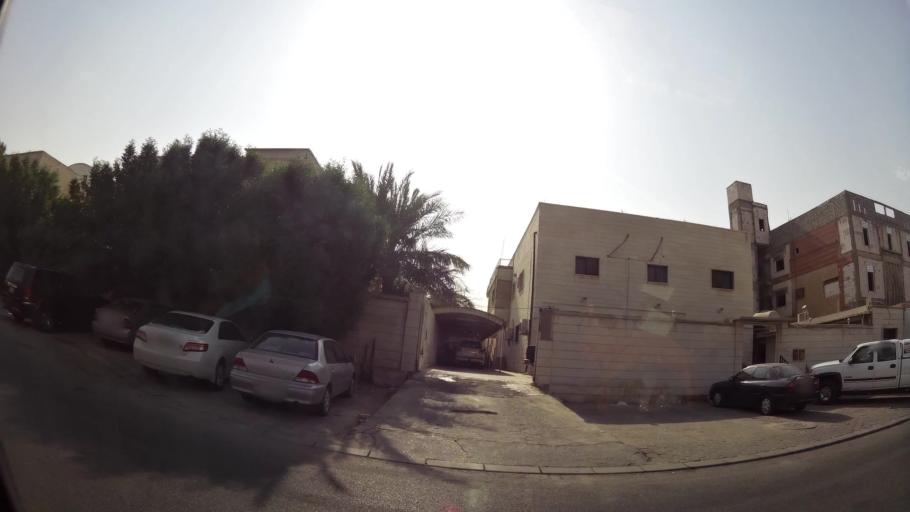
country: KW
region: Muhafazat al Jahra'
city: Al Jahra'
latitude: 29.3549
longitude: 47.6771
